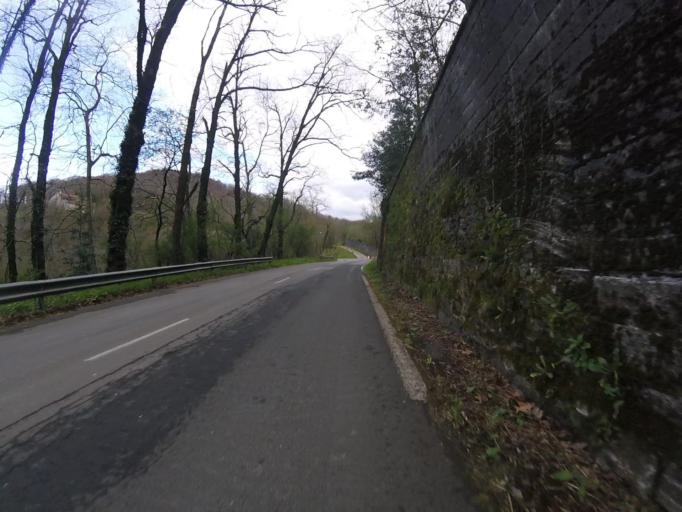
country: ES
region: Basque Country
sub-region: Provincia de Guipuzcoa
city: Errenteria
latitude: 43.2883
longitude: -1.8564
